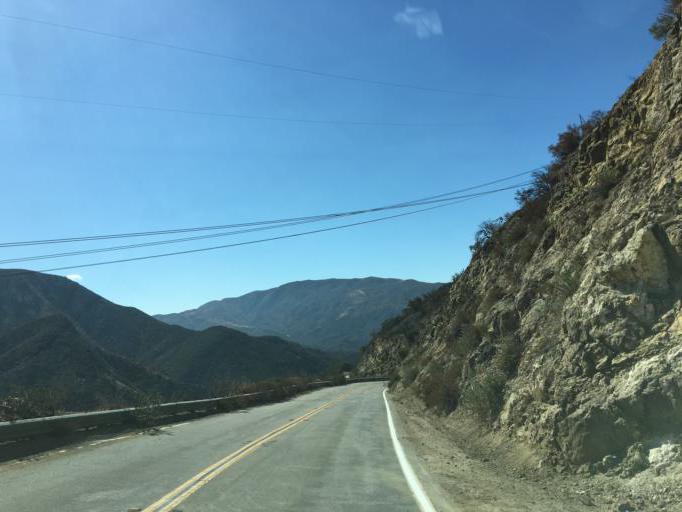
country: US
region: California
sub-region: Los Angeles County
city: San Fernando
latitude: 34.3379
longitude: -118.3403
